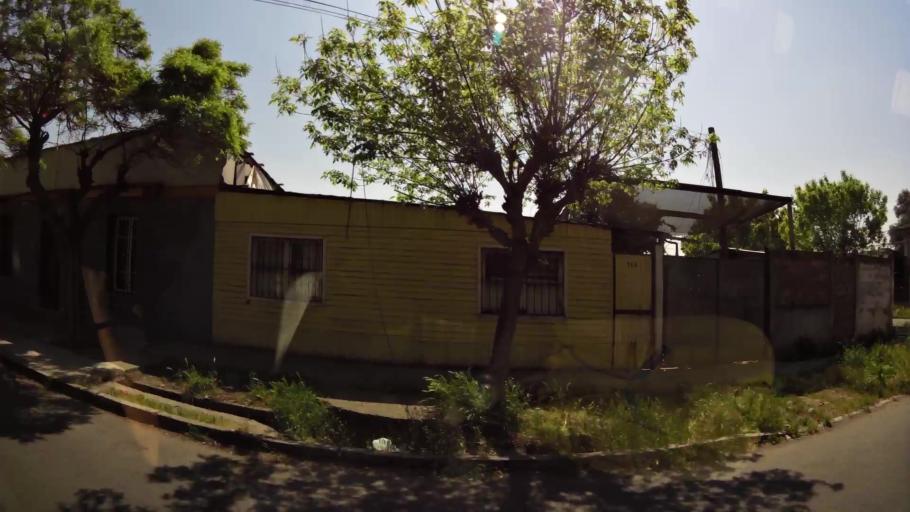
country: CL
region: Santiago Metropolitan
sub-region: Provincia de Maipo
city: San Bernardo
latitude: -33.6025
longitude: -70.7124
